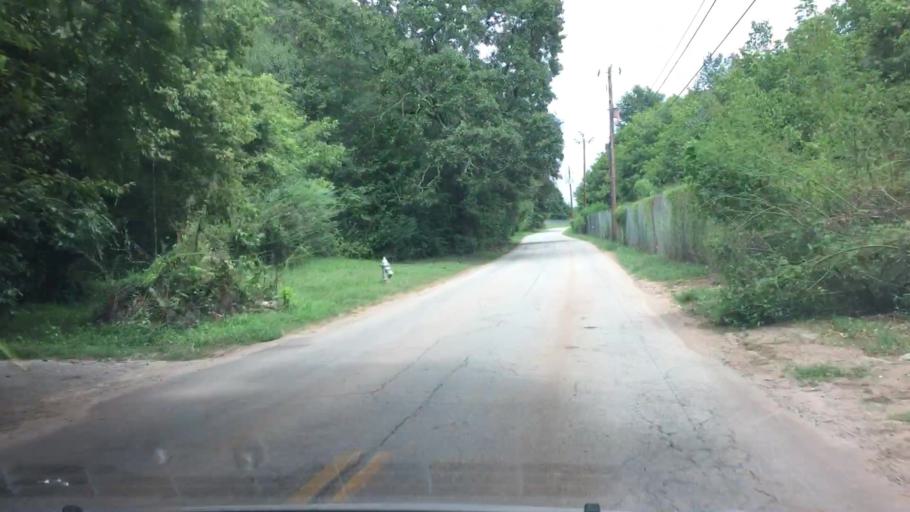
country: US
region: Georgia
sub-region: DeKalb County
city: Gresham Park
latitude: 33.6964
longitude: -84.3405
